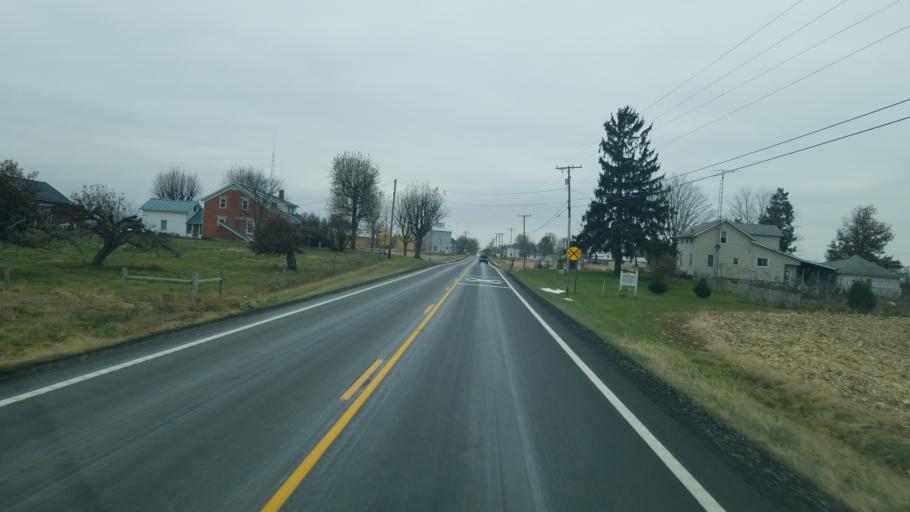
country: US
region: Ohio
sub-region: Crawford County
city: Bucyrus
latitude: 40.9604
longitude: -82.9391
